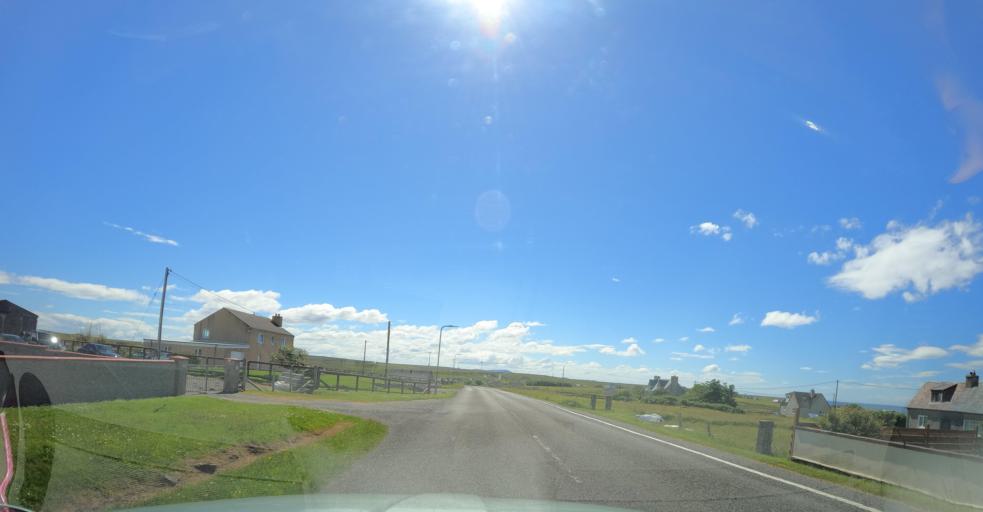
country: GB
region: Scotland
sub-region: Eilean Siar
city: Isle of Lewis
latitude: 58.4007
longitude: -6.4678
